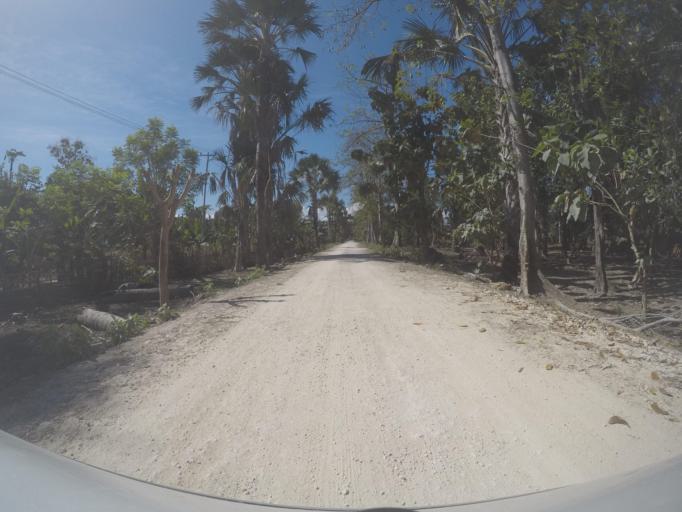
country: TL
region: Viqueque
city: Viqueque
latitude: -8.9030
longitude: 126.5059
